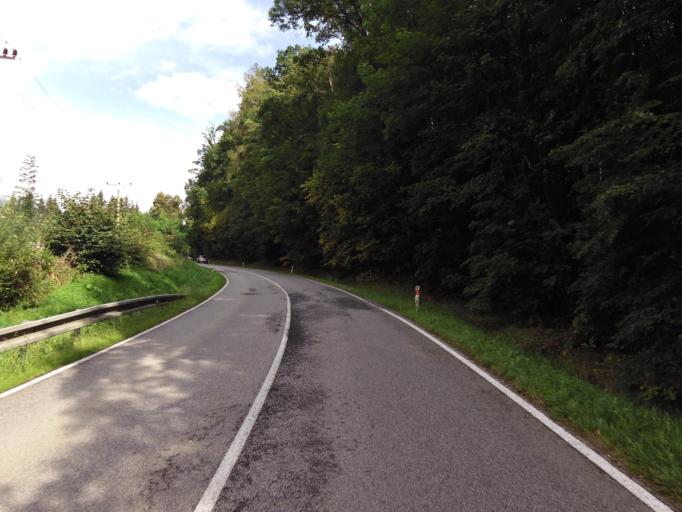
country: CZ
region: Jihocesky
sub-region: Okres Ceske Budejovice
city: Nove Hrady
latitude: 48.7936
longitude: 14.7786
